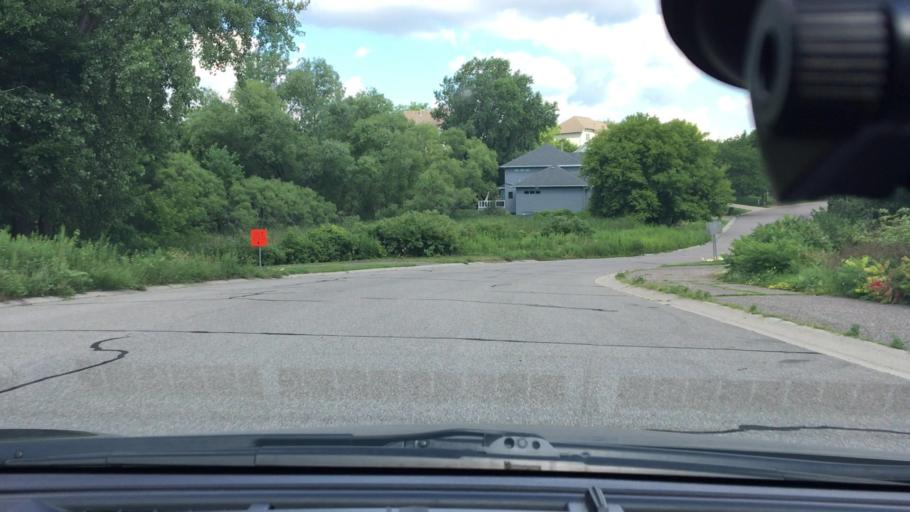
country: US
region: Minnesota
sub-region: Hennepin County
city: Plymouth
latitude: 45.0325
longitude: -93.4458
